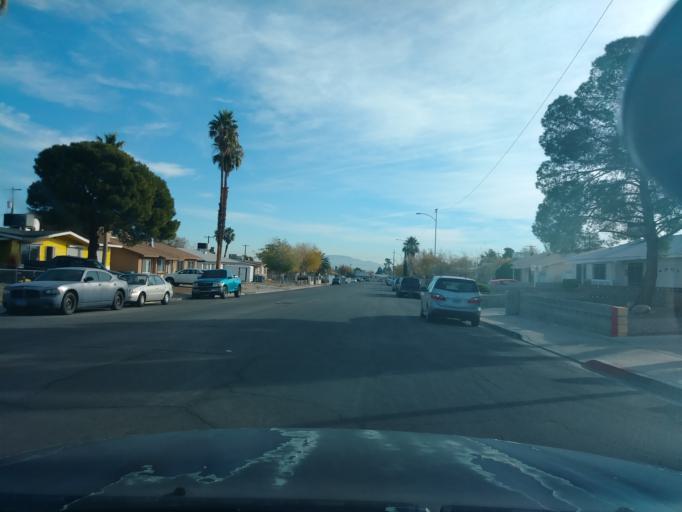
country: US
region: Nevada
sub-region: Clark County
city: Spring Valley
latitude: 36.1622
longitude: -115.2331
